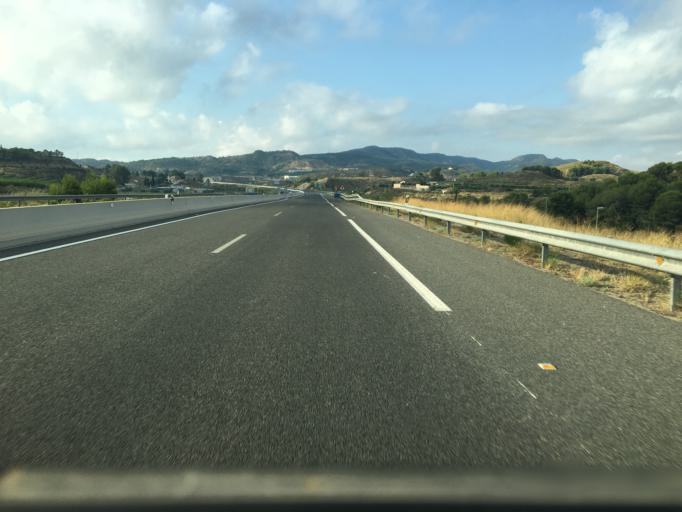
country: ES
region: Murcia
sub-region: Murcia
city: Beniel
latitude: 37.9792
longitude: -0.9747
